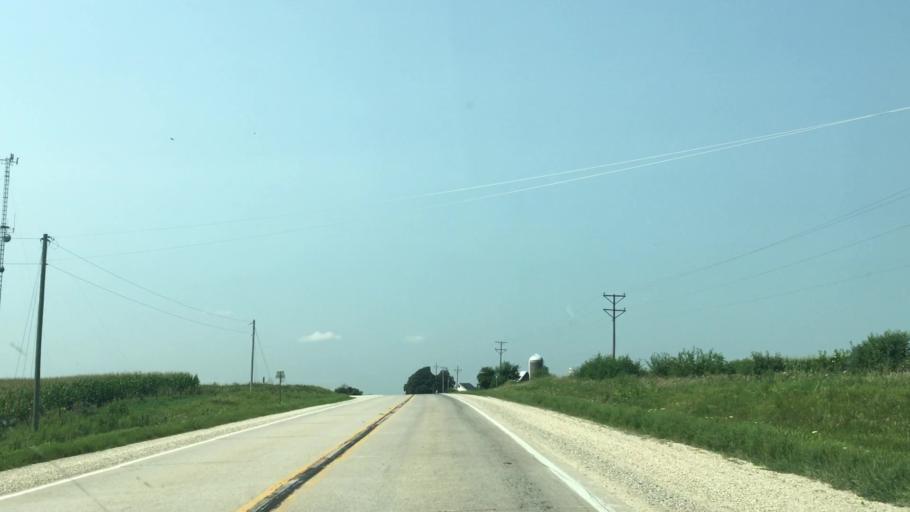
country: US
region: Iowa
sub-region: Fayette County
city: West Union
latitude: 43.0892
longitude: -91.8524
